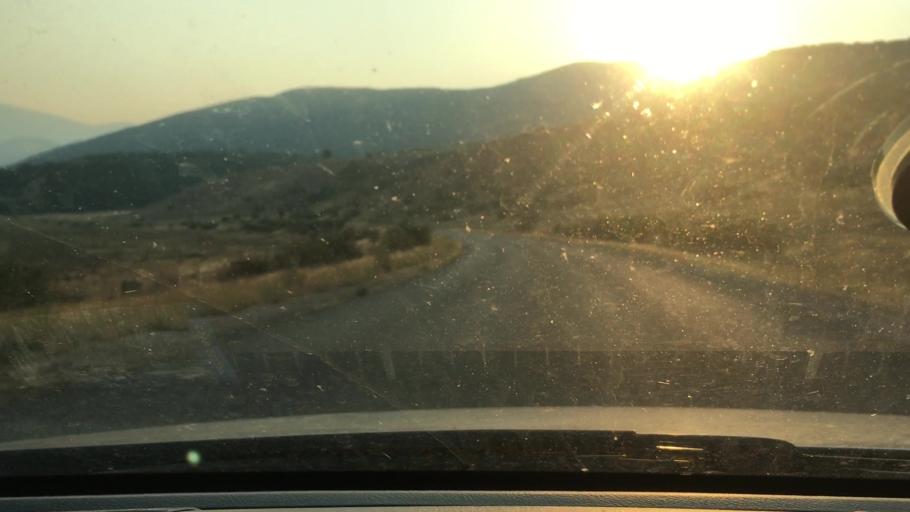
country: US
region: Utah
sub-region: Utah County
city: Mapleton
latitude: 40.0442
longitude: -111.4710
